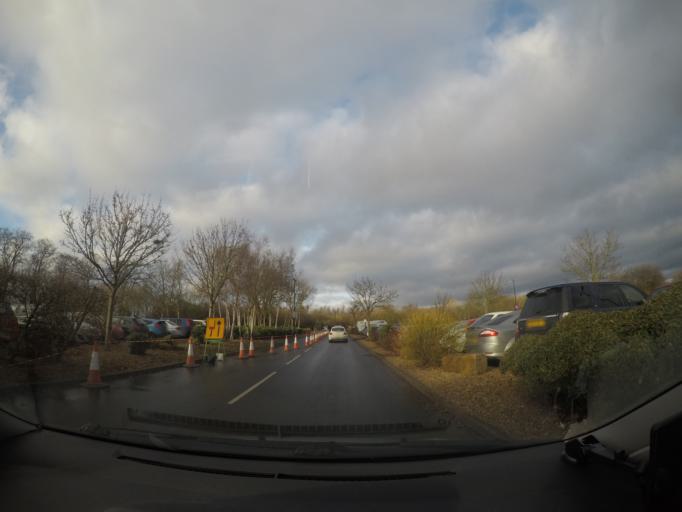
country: GB
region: England
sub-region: City of York
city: Fulford
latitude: 53.9241
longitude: -1.0776
